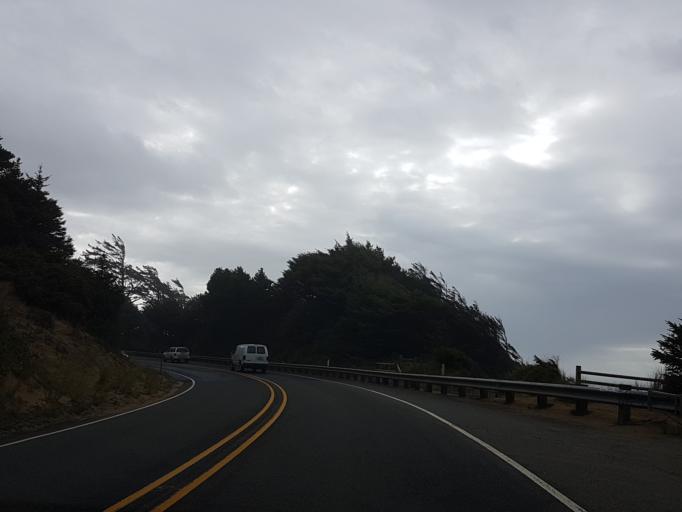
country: US
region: Oregon
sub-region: Lincoln County
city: Waldport
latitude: 44.2814
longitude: -124.1090
